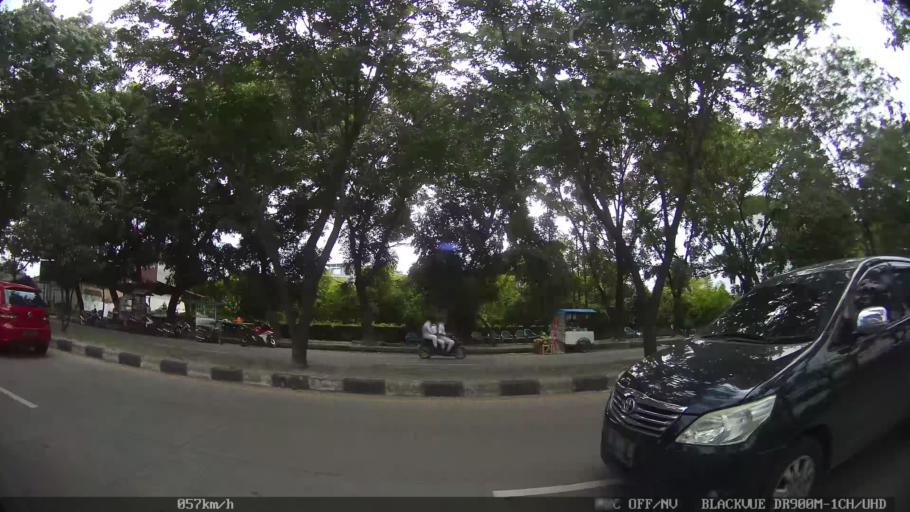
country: ID
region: North Sumatra
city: Medan
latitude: 3.6301
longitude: 98.6756
